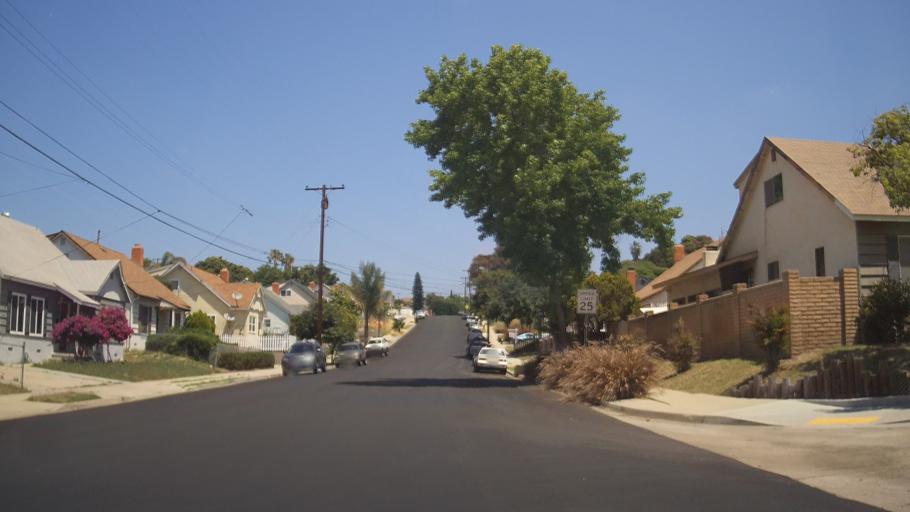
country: US
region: California
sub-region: San Diego County
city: Bonita
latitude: 32.6711
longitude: -117.0476
